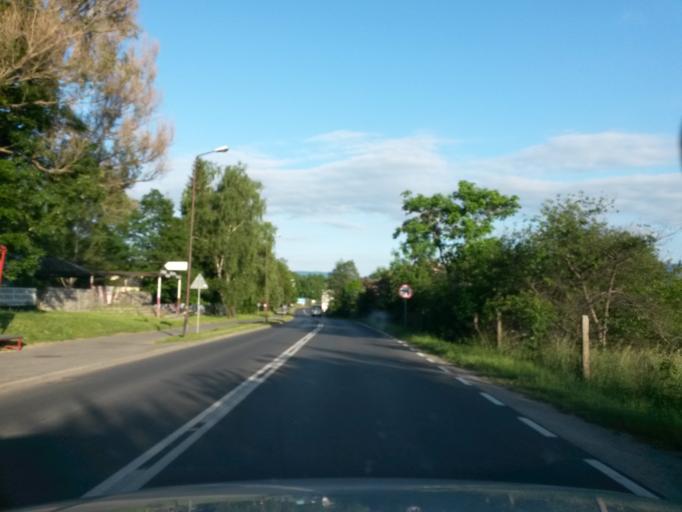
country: PL
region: Lower Silesian Voivodeship
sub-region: Jelenia Gora
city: Jelenia Gora
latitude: 50.8902
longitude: 15.7506
